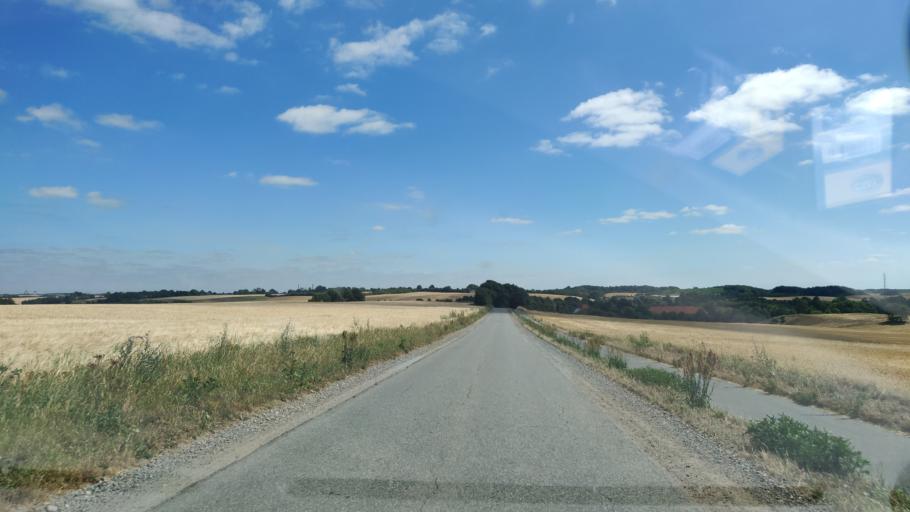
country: DK
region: South Denmark
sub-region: Kolding Kommune
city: Kolding
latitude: 55.5351
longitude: 9.5287
